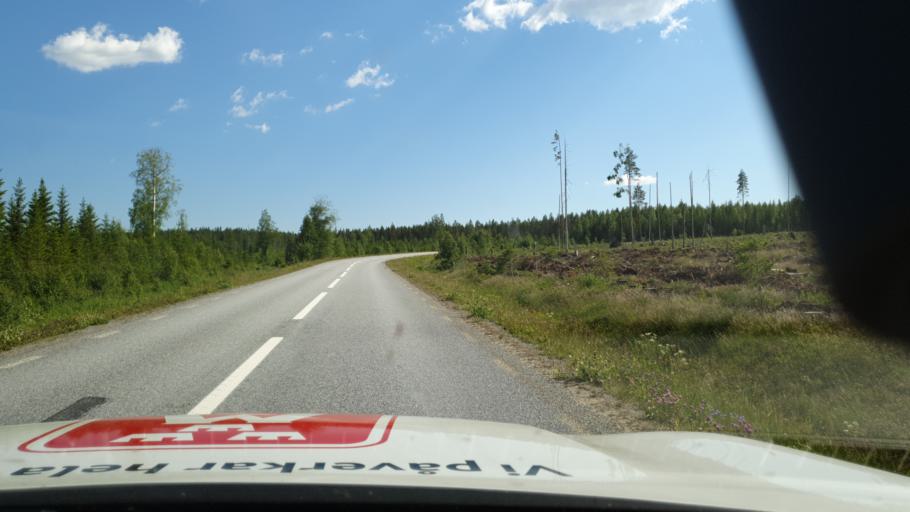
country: SE
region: Vaesterbotten
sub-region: Skelleftea Kommun
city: Burtraesk
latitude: 64.4148
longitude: 20.3964
